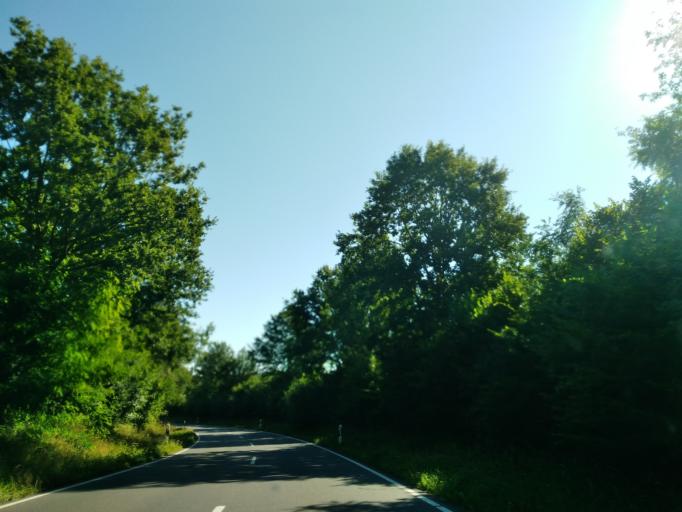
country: DE
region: Baden-Wuerttemberg
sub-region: Karlsruhe Region
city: Limbach
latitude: 49.4984
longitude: 9.2639
